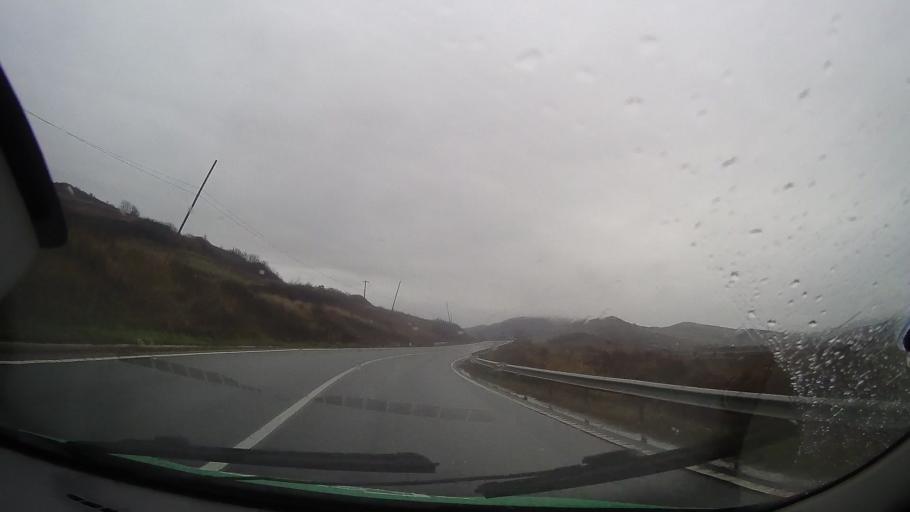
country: RO
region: Bistrita-Nasaud
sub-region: Comuna Galatii Bistritei
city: Galatii Bistritei
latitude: 46.9558
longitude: 24.4434
